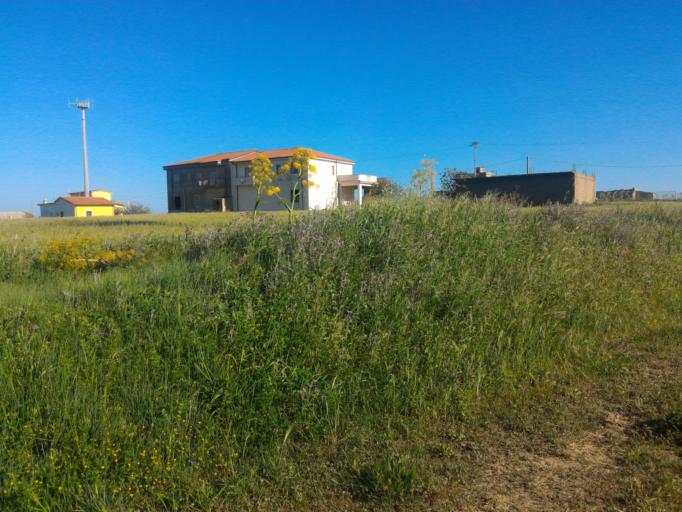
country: IT
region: Calabria
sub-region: Provincia di Crotone
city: Crotone
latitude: 39.0330
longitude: 17.1603
